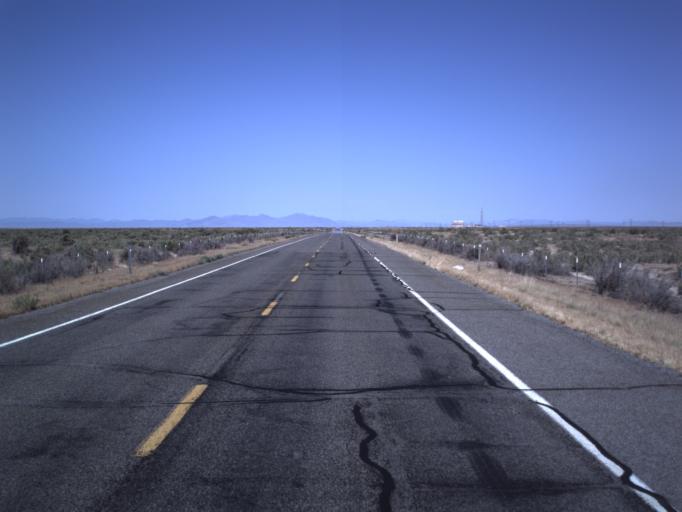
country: US
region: Utah
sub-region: Millard County
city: Delta
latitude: 39.4709
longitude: -112.4635
